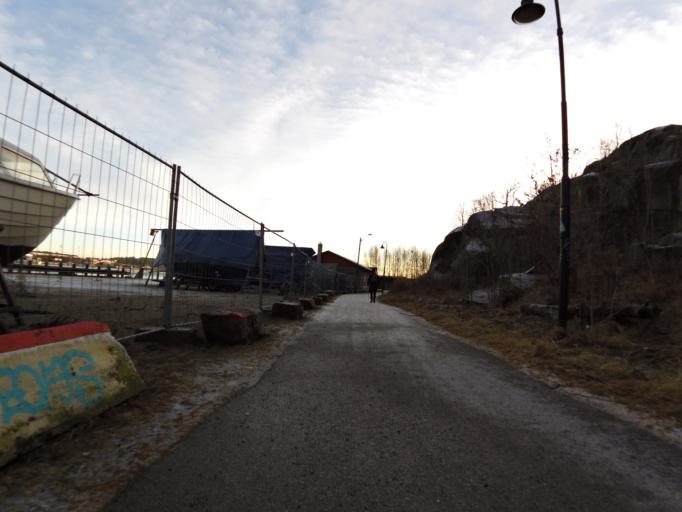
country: NO
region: Ostfold
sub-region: Fredrikstad
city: Fredrikstad
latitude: 59.2199
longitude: 10.9146
